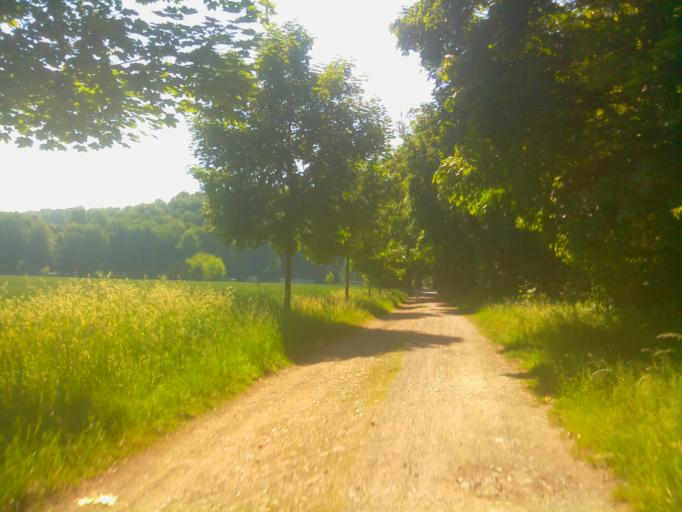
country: DE
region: Thuringia
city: Rudolstadt
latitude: 50.7098
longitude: 11.3252
